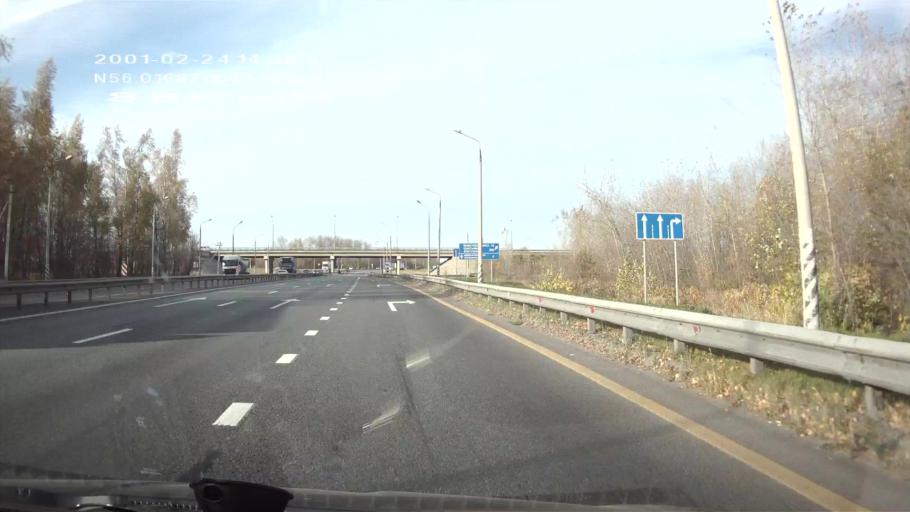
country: RU
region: Chuvashia
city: Kugesi
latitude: 56.0168
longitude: 47.3085
